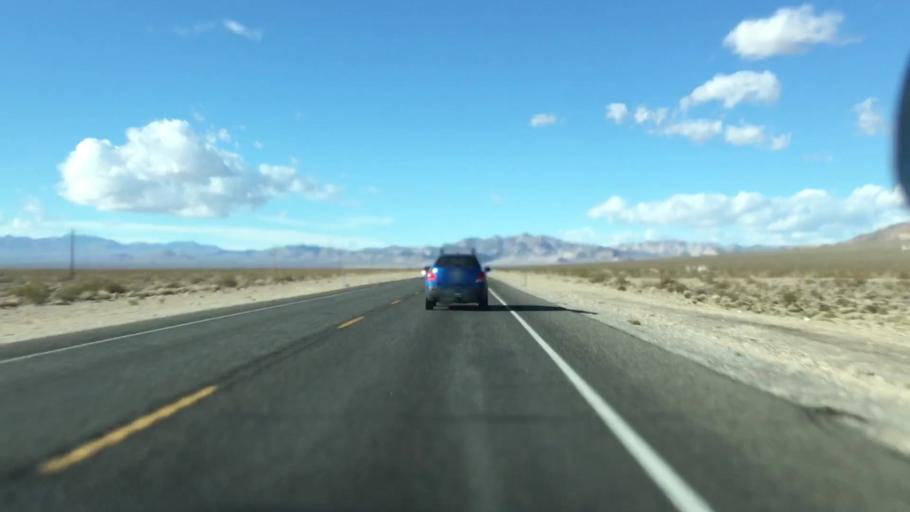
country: US
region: Nevada
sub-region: Nye County
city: Beatty
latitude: 36.7960
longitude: -116.7113
